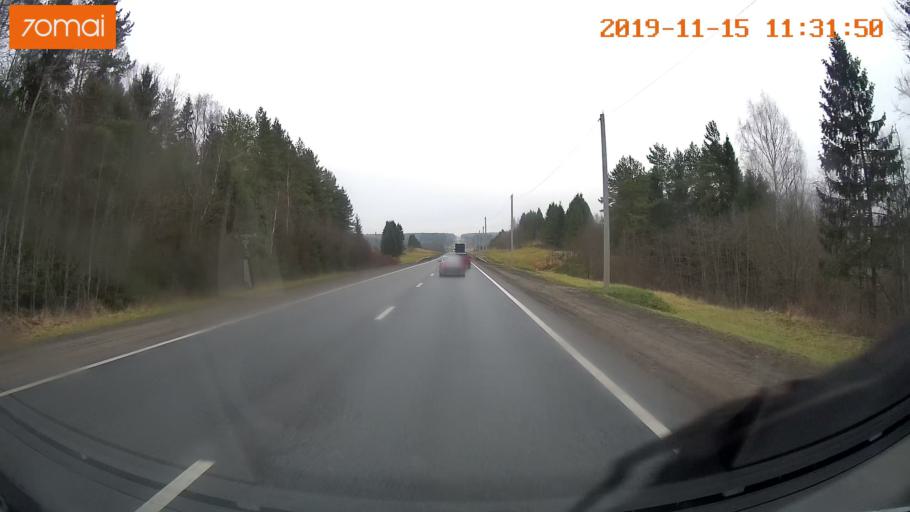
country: RU
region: Vologda
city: Molochnoye
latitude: 59.1831
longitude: 39.5620
